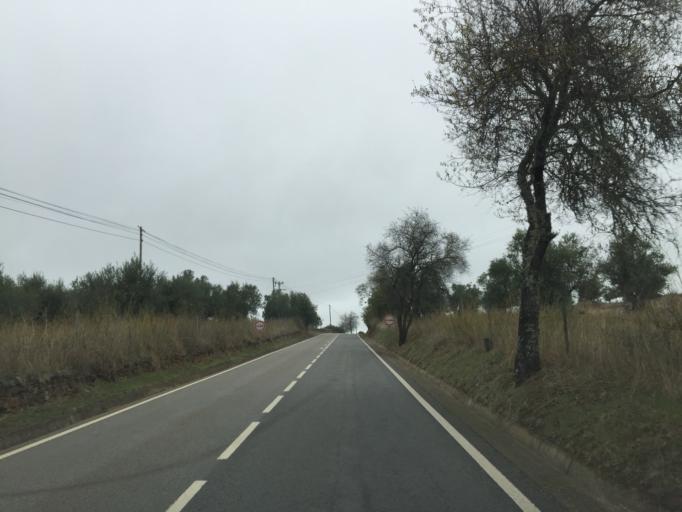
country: PT
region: Portalegre
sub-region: Alter do Chao
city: Alter do Chao
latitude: 39.2098
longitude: -7.6564
